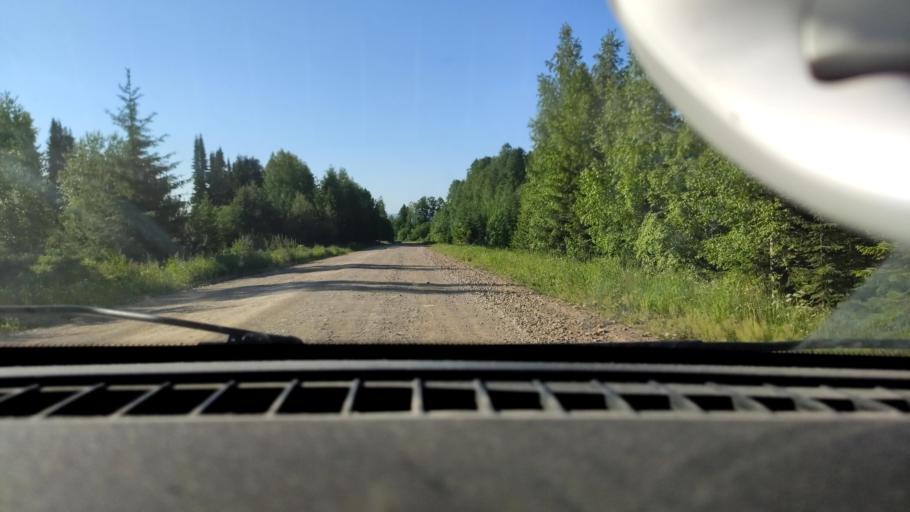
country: RU
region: Perm
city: Novyye Lyady
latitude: 58.1766
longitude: 56.5922
